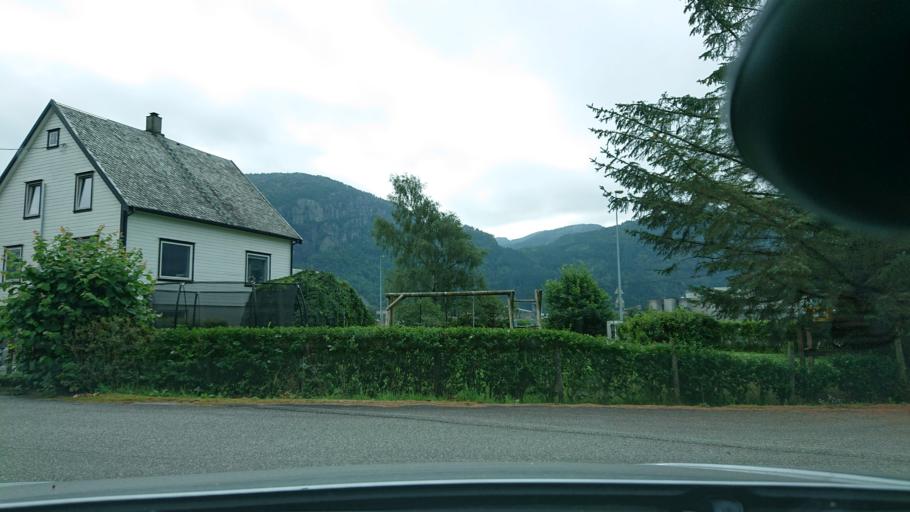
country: NO
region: Rogaland
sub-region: Hjelmeland
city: Hjelmelandsvagen
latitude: 59.1507
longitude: 6.1678
